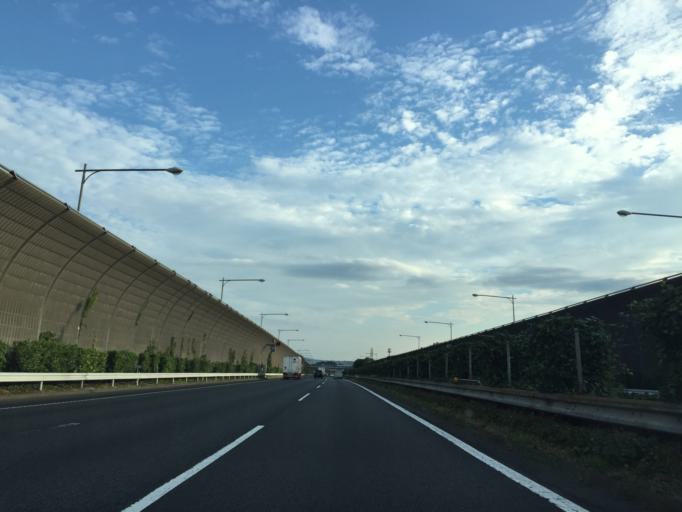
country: JP
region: Kanagawa
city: Isehara
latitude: 35.3987
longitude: 139.2866
